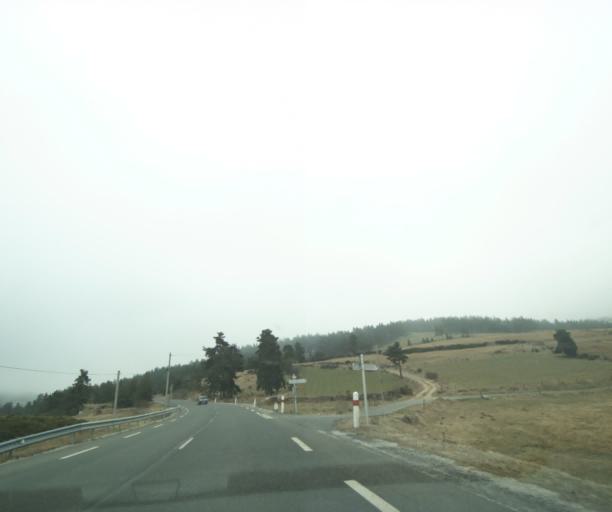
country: FR
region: Languedoc-Roussillon
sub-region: Departement de la Lozere
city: Langogne
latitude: 44.6650
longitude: 3.7607
